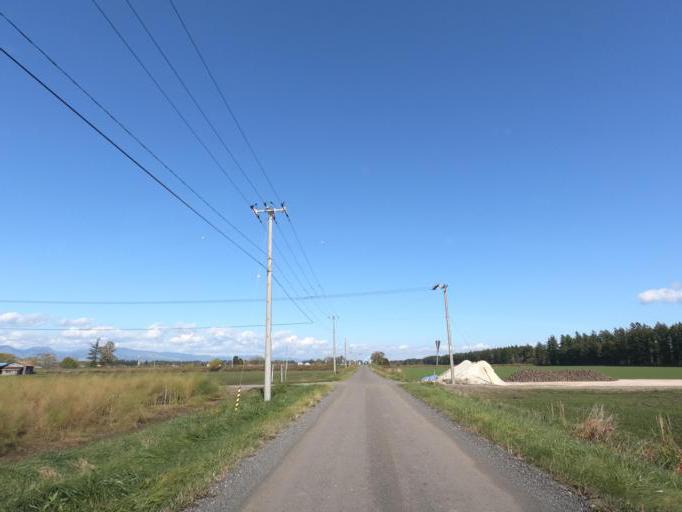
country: JP
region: Hokkaido
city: Otofuke
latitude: 43.0813
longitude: 143.2610
